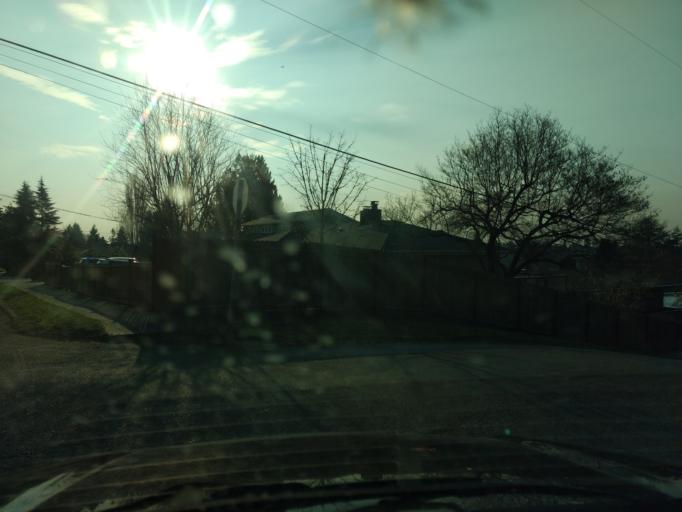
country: US
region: Washington
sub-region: King County
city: Lake Forest Park
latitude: 47.6885
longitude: -122.2961
